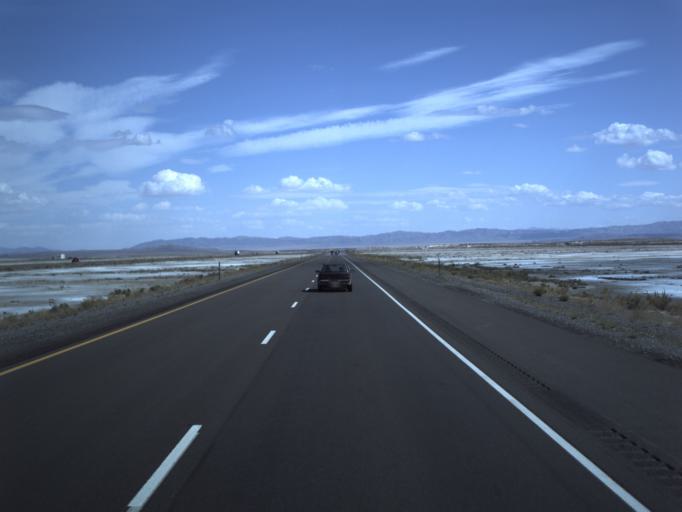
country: US
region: Utah
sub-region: Tooele County
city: Wendover
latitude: 40.7273
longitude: -113.3108
